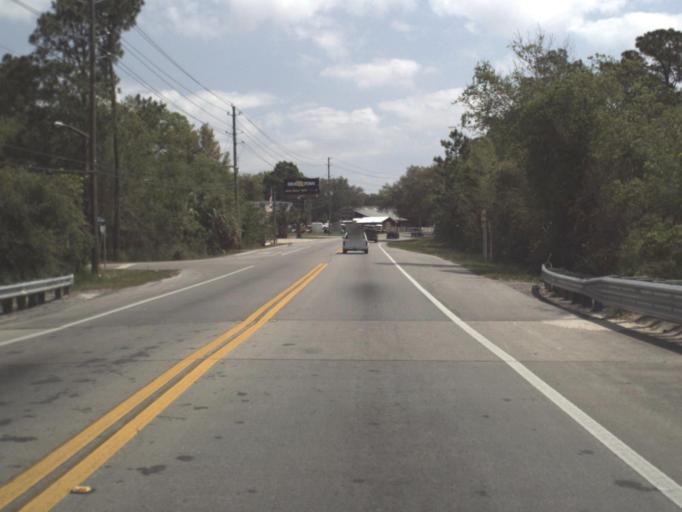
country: US
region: Florida
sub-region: Escambia County
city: Warrington
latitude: 30.3774
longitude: -87.3166
